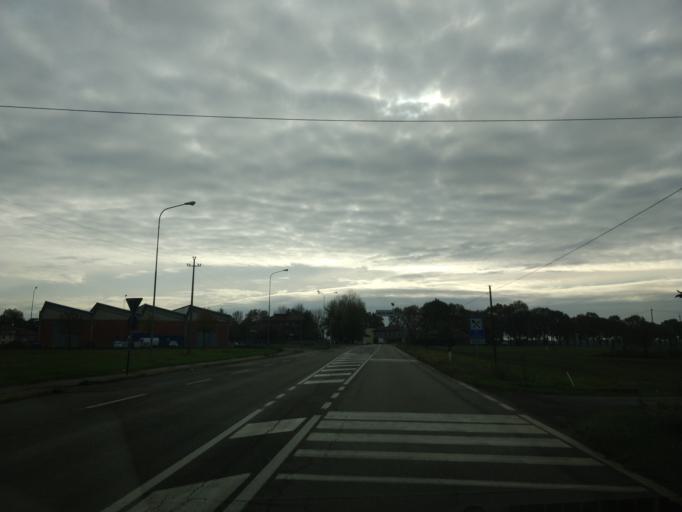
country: IT
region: Emilia-Romagna
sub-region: Provincia di Bologna
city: Castello d'Argile
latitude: 44.6688
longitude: 11.3041
